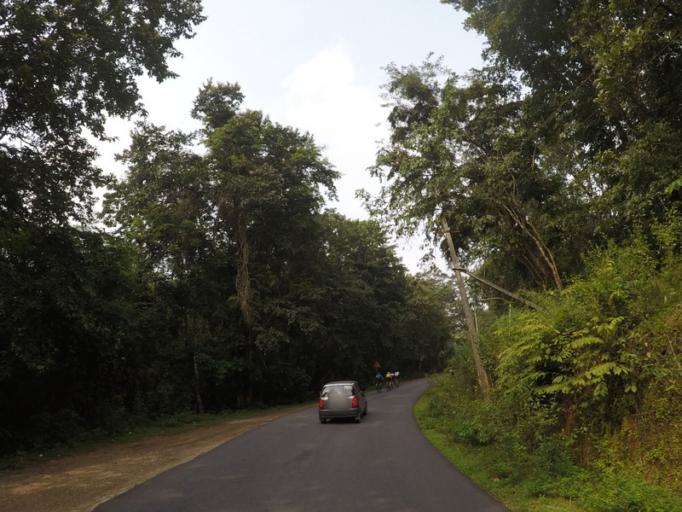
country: IN
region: Karnataka
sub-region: Chikmagalur
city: Koppa
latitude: 13.3526
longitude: 75.4892
